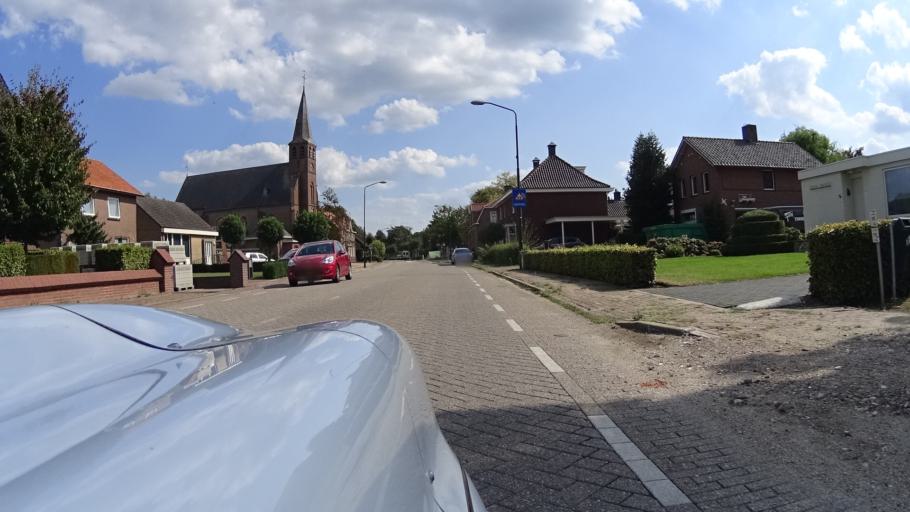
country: NL
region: North Brabant
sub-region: Gemeente Sint Anthonis
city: Sint Anthonis
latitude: 51.6365
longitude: 5.8726
